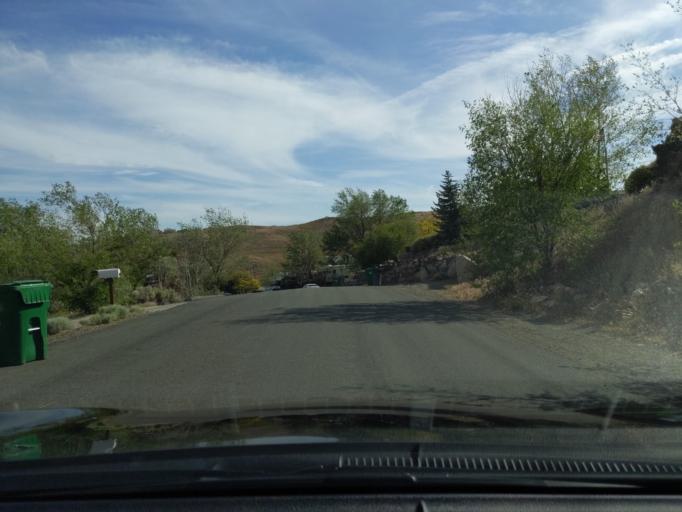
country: US
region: Nevada
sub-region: Washoe County
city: Sun Valley
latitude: 39.5721
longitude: -119.7842
